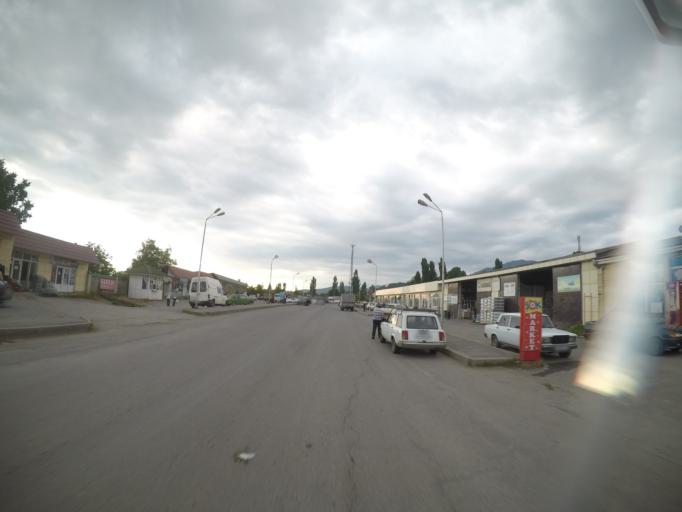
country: AZ
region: Qabala Rayon
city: Qutqashen
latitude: 40.9451
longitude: 47.9442
